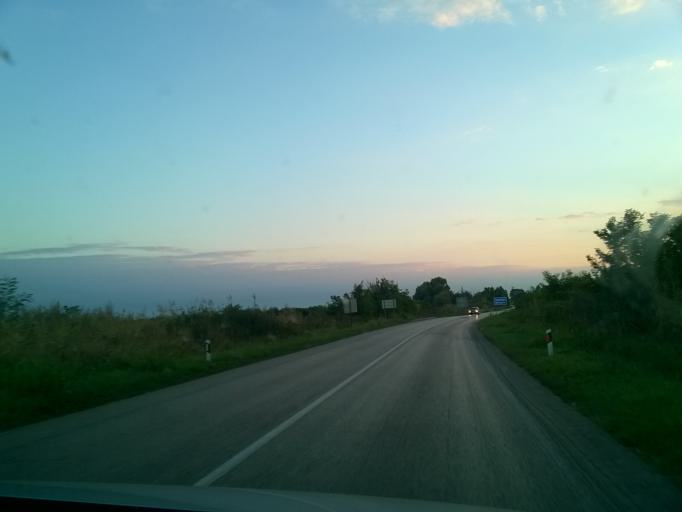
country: RS
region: Autonomna Pokrajina Vojvodina
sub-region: Juznobanatski Okrug
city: Pancevo
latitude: 44.9370
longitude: 20.6698
